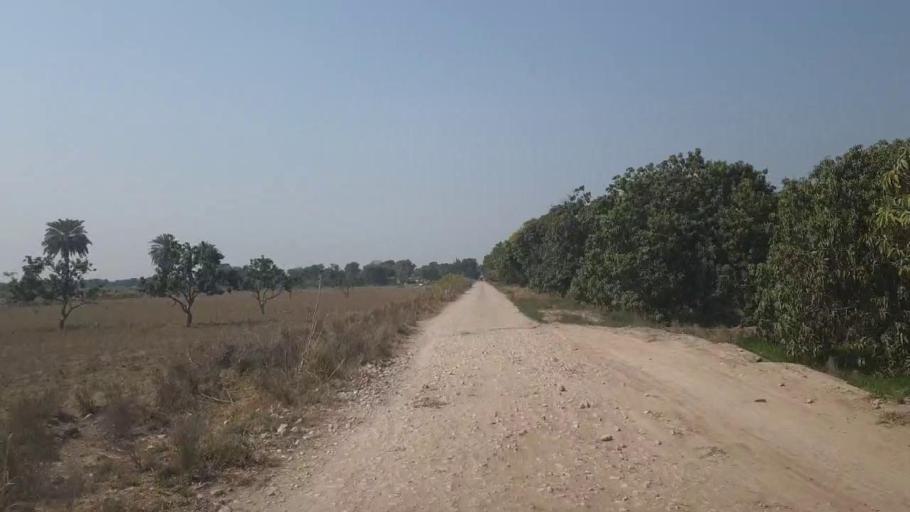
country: PK
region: Sindh
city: Tando Allahyar
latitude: 25.4598
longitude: 68.8083
